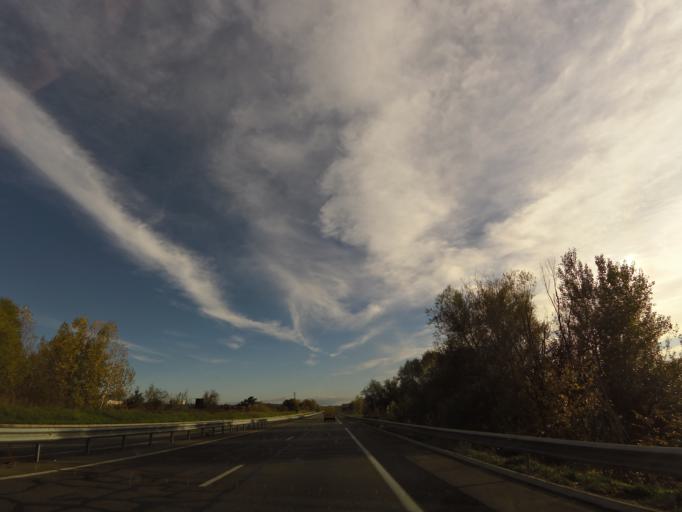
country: FR
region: Languedoc-Roussillon
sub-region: Departement du Gard
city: Saint-Hilaire-de-Brethmas
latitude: 44.0874
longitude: 4.1078
